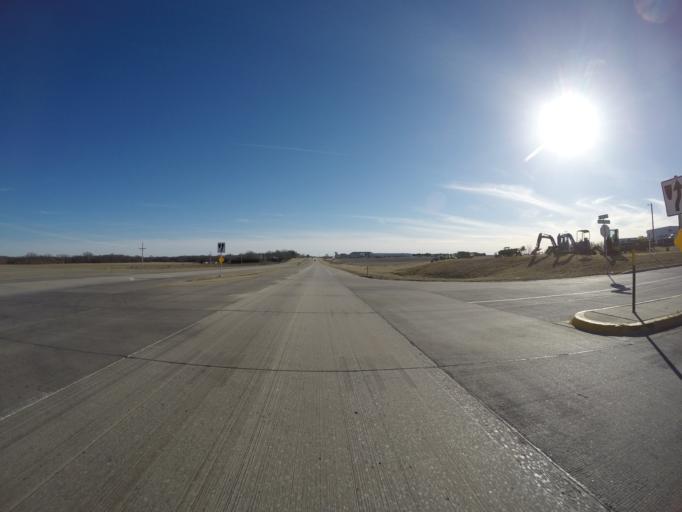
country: US
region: Nebraska
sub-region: Gage County
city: Beatrice
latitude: 40.3138
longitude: -96.7471
